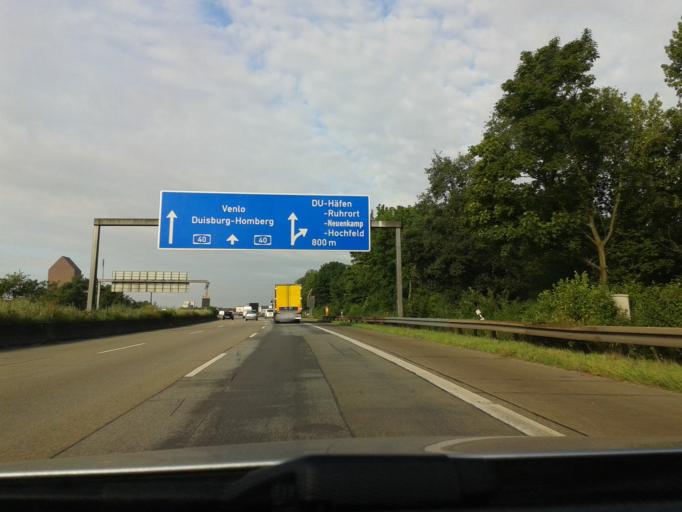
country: DE
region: North Rhine-Westphalia
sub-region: Regierungsbezirk Dusseldorf
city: Duisburg
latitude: 51.4432
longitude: 6.7649
